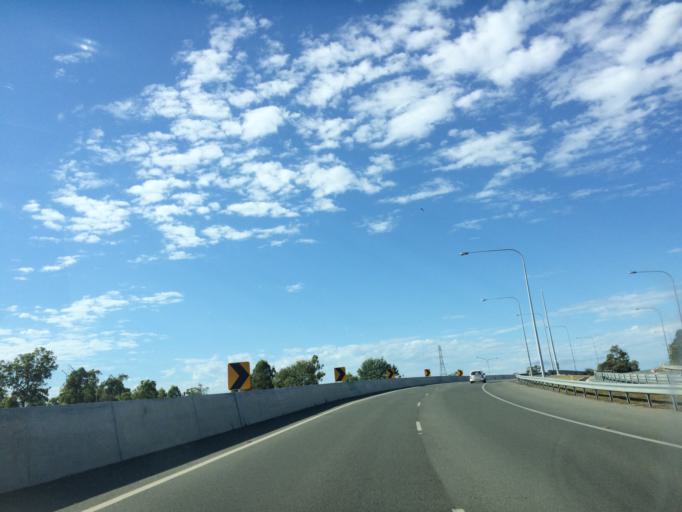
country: AU
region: Queensland
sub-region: Brisbane
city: Forest Lake
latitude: -27.6237
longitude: 152.9431
